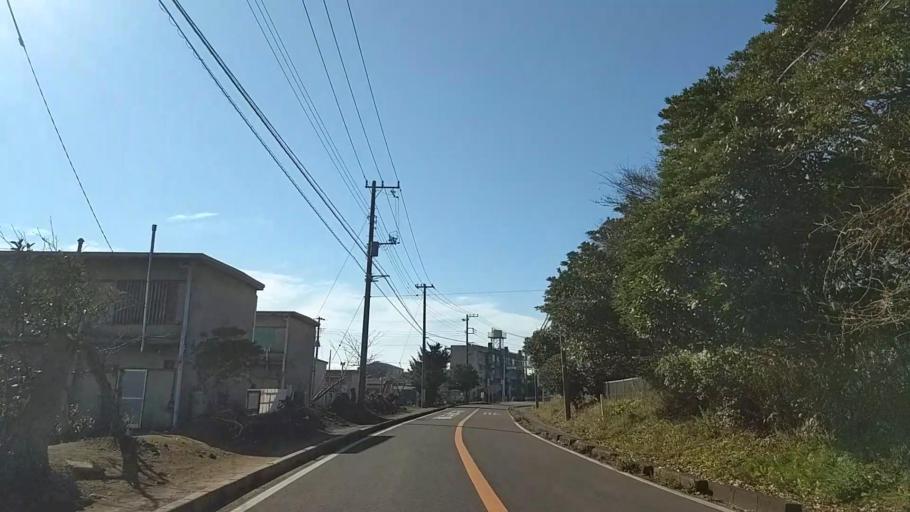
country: JP
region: Chiba
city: Hasaki
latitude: 35.7021
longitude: 140.8588
